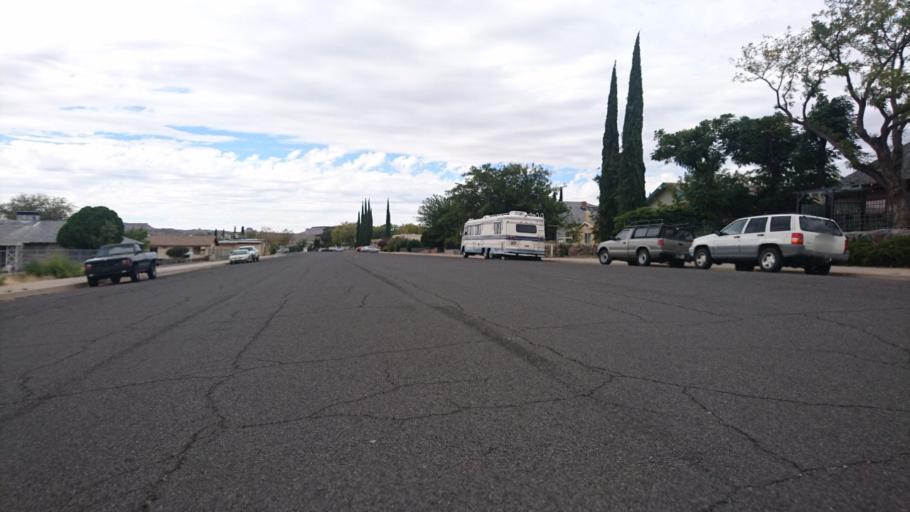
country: US
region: Arizona
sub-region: Mohave County
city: Kingman
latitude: 35.1901
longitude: -114.0493
